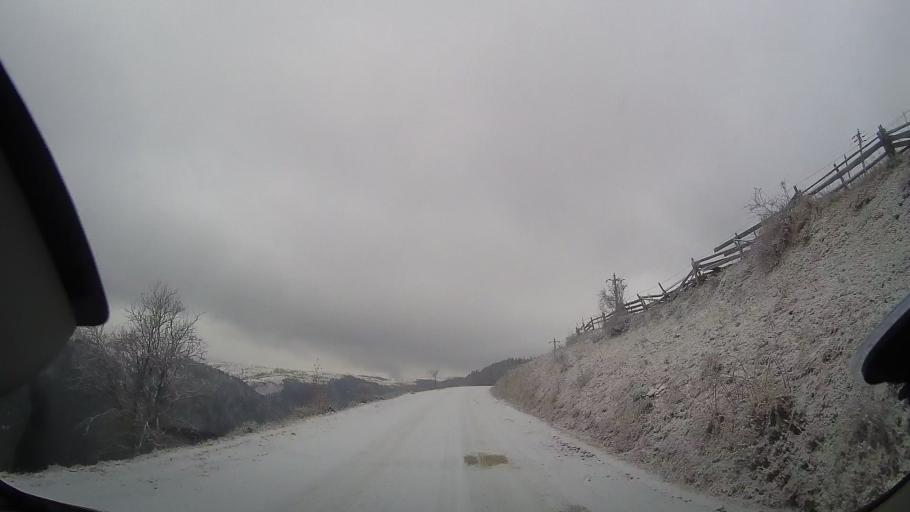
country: RO
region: Cluj
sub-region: Comuna Marisel
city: Marisel
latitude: 46.6622
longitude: 23.1566
